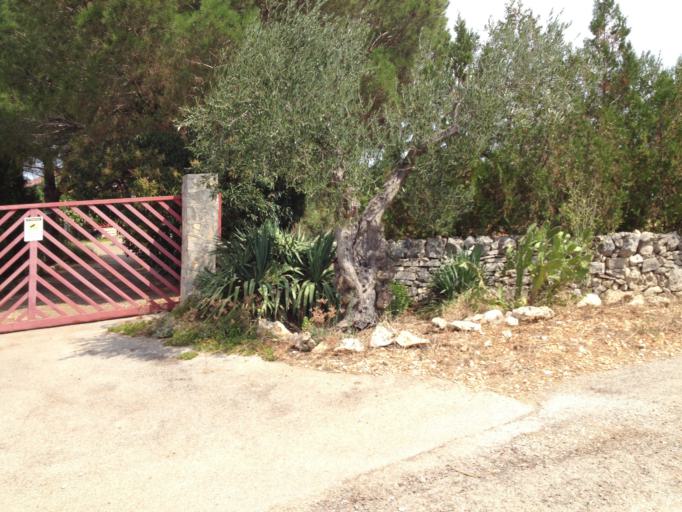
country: IT
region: Apulia
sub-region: Provincia di Bari
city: Gioia del Colle
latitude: 40.8256
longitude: 16.9798
